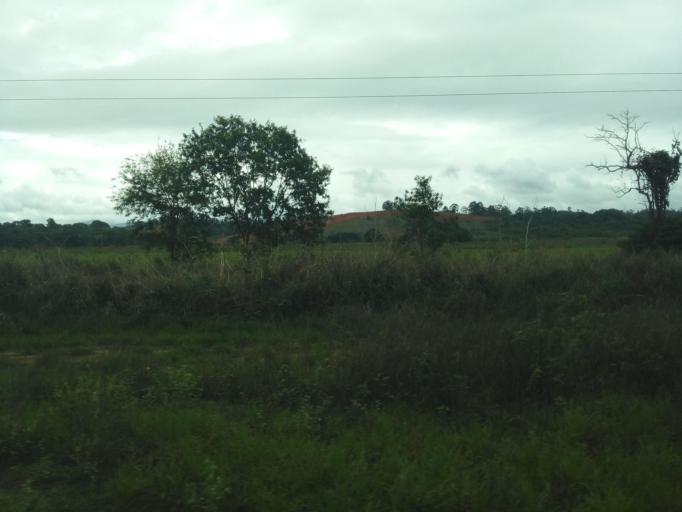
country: BR
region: Minas Gerais
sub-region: Ipatinga
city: Ipatinga
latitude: -19.4706
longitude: -42.4816
